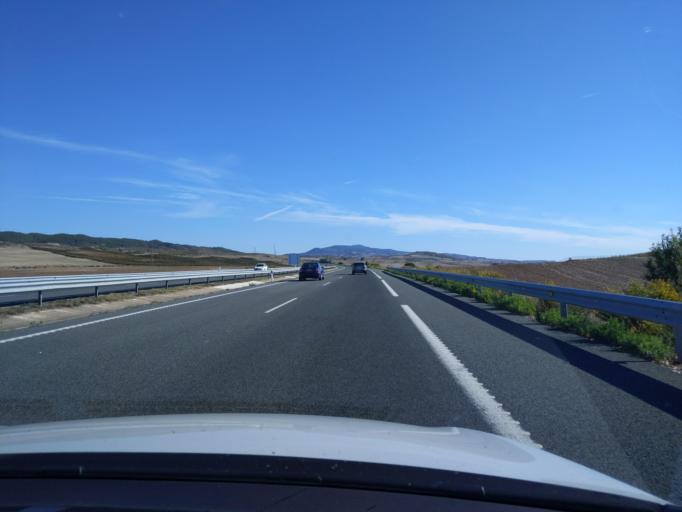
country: ES
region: Navarre
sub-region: Provincia de Navarra
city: Los Arcos
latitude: 42.5663
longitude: -2.1703
